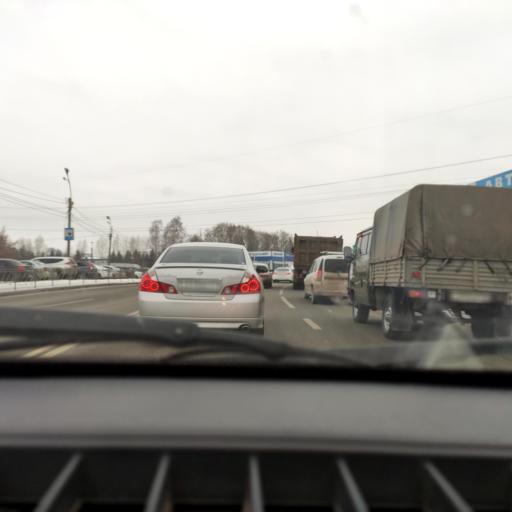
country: RU
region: Bashkortostan
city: Ufa
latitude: 54.7992
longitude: 56.0757
